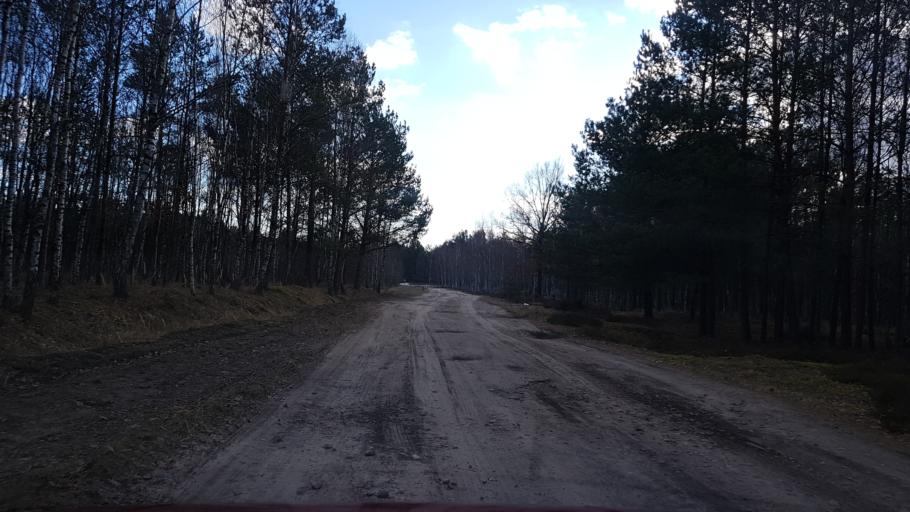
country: PL
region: Greater Poland Voivodeship
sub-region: Powiat zlotowski
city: Sypniewo
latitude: 53.5240
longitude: 16.6474
